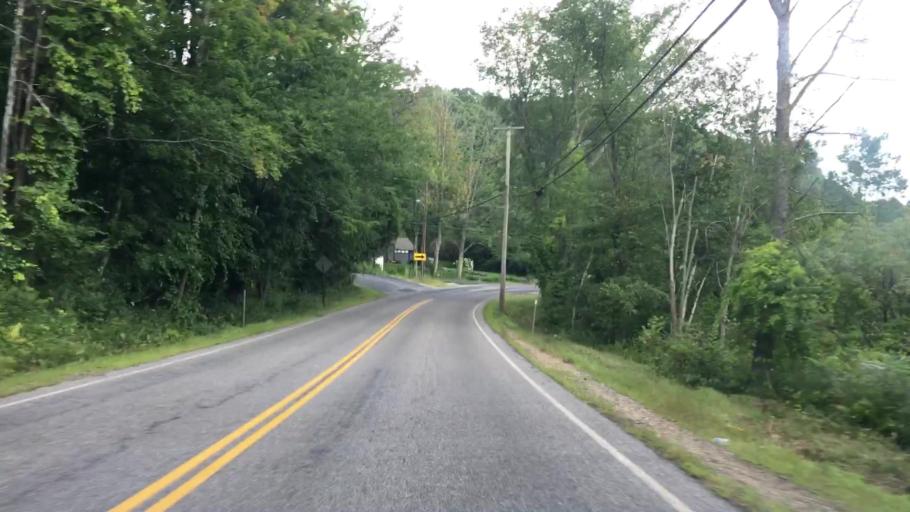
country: US
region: New Hampshire
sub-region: Belknap County
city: Sanbornton
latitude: 43.4923
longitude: -71.5844
